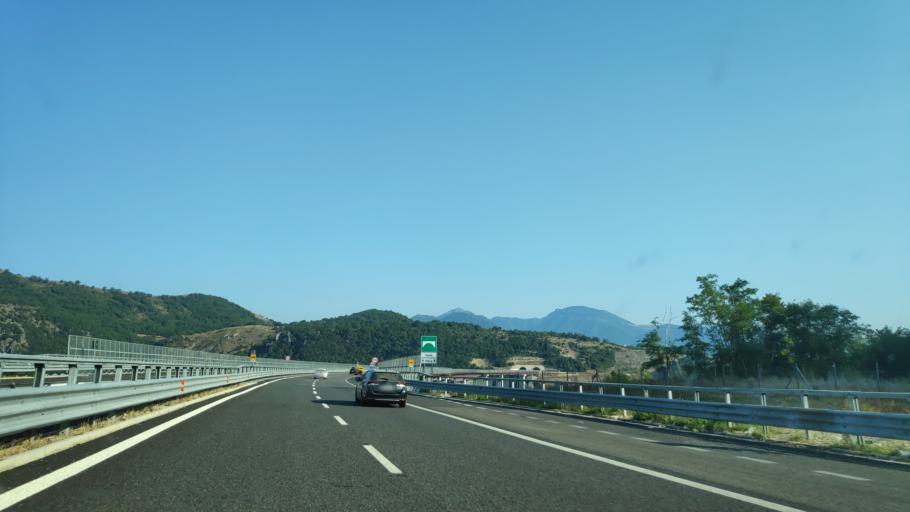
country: IT
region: Calabria
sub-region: Provincia di Cosenza
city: Laino Castello-Nuovo Centro
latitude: 39.9332
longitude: 15.9620
